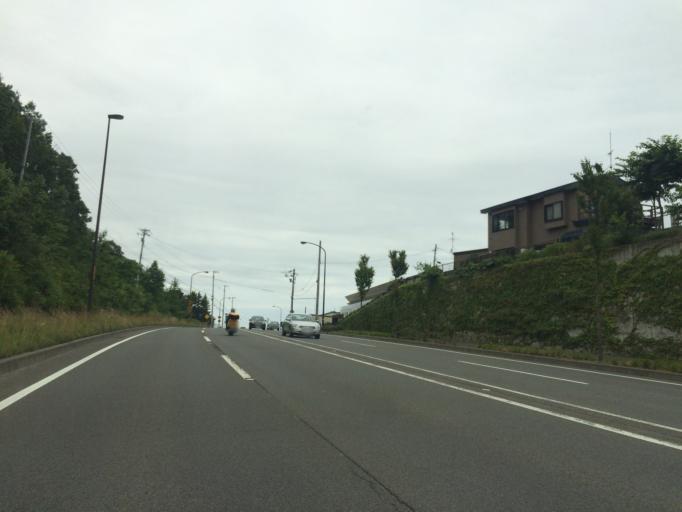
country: JP
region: Hokkaido
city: Otaru
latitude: 43.1467
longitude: 141.1386
